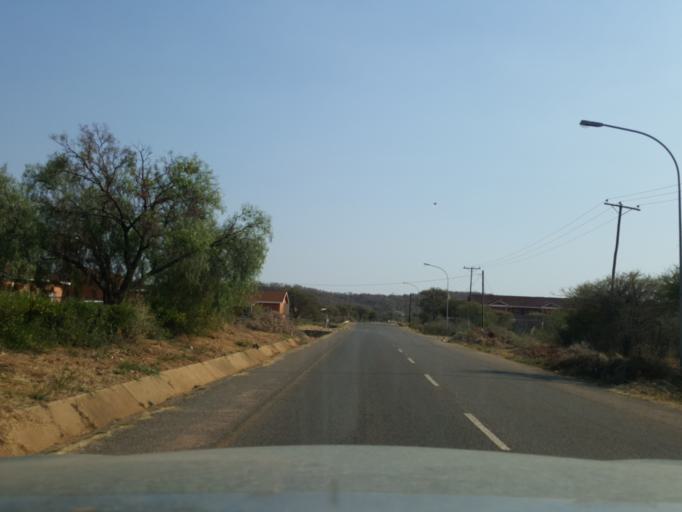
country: BW
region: South East
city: Lobatse
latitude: -25.1894
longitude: 25.6945
